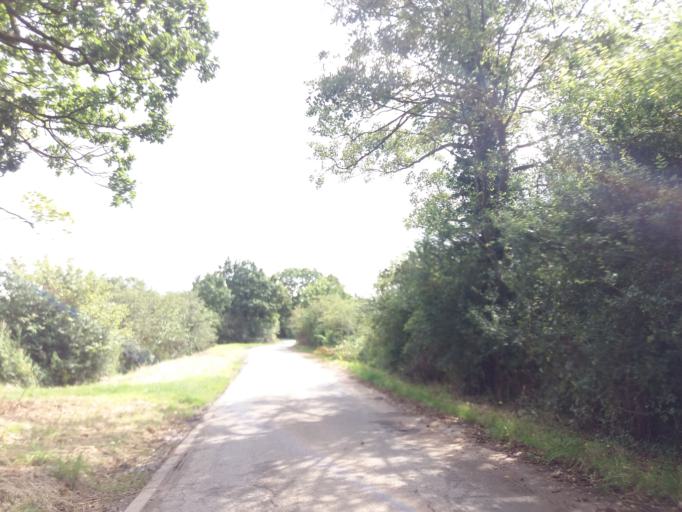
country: GB
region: England
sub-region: Lancashire
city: Euxton
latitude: 53.6689
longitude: -2.6671
